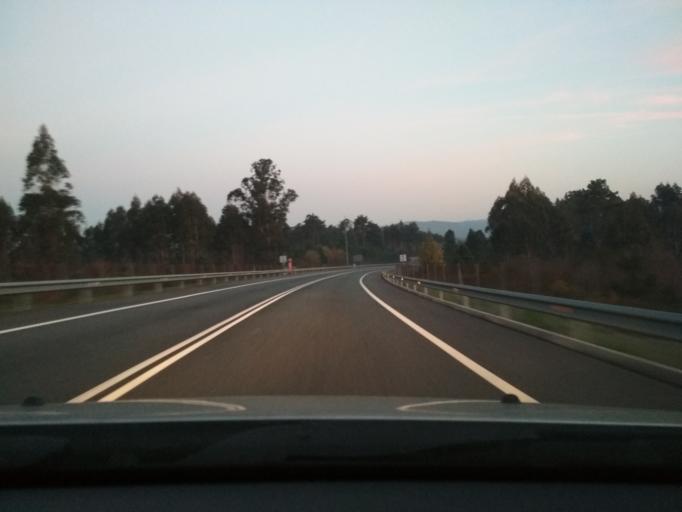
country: ES
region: Galicia
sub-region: Provincia da Coruna
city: Ames
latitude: 42.8511
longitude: -8.5996
